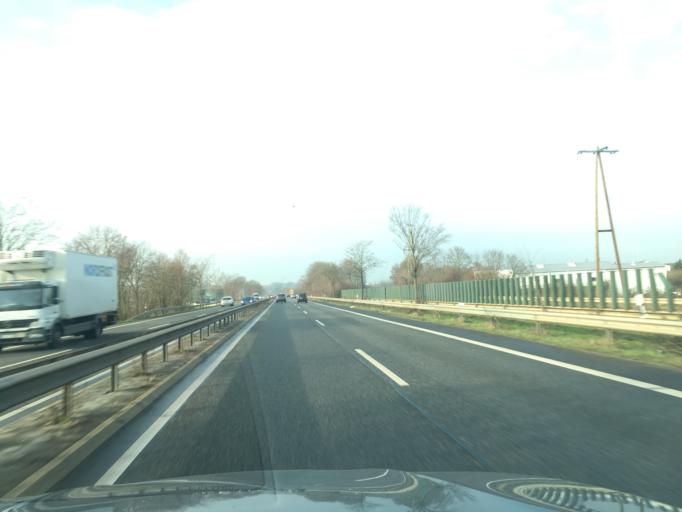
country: DE
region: Rheinland-Pfalz
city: Mulheim-Karlich
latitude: 50.4024
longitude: 7.4896
